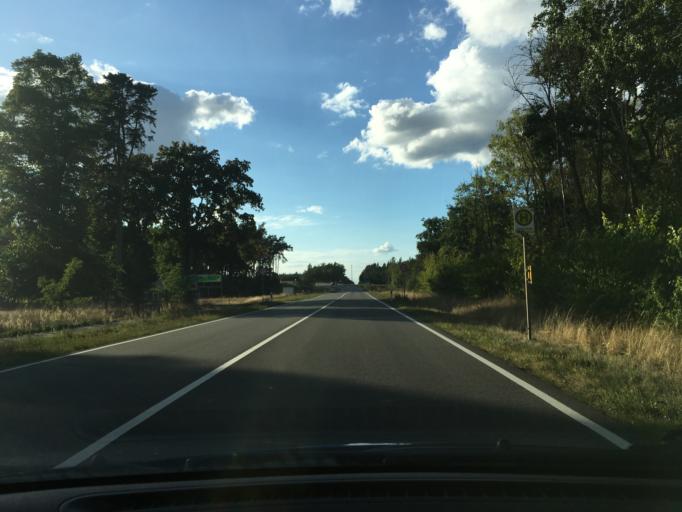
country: DE
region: Mecklenburg-Vorpommern
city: Grabow
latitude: 53.2977
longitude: 11.5348
